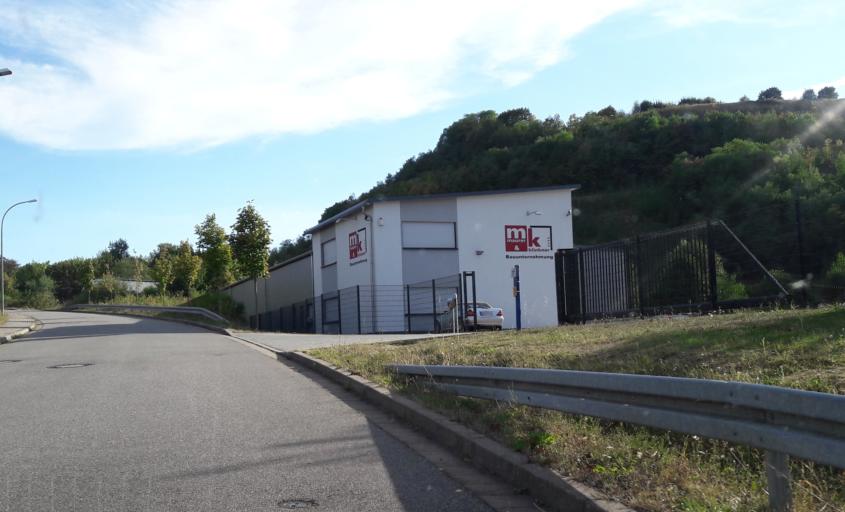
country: DE
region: Saarland
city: Schiffweiler
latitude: 49.3494
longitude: 7.1273
